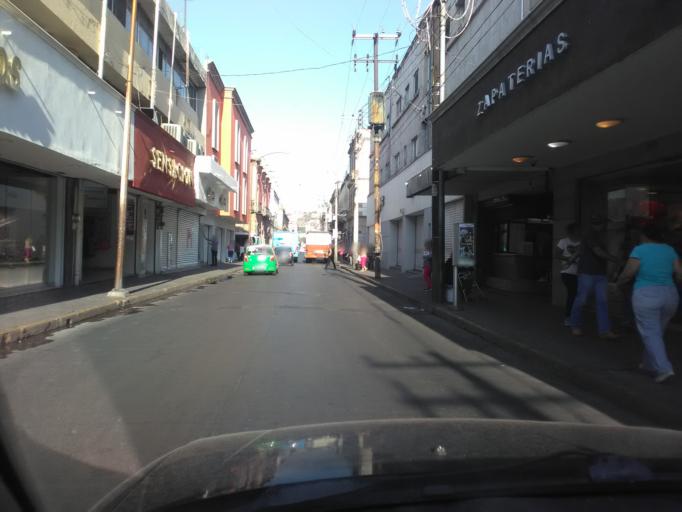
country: MX
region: Durango
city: Victoria de Durango
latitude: 24.0238
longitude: -104.6678
